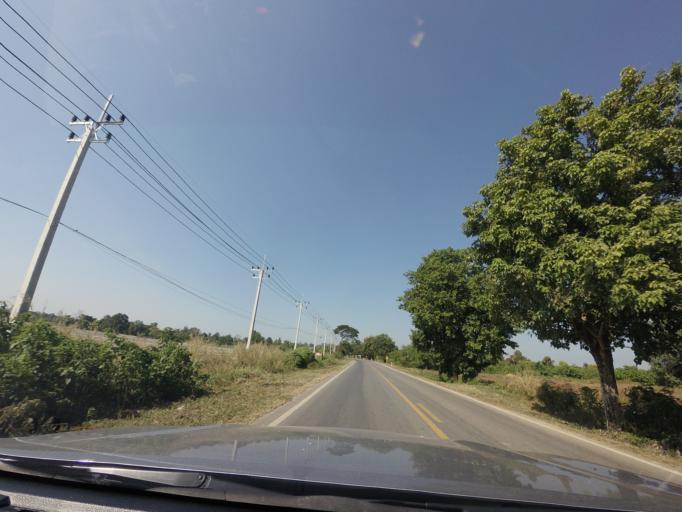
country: TH
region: Sukhothai
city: Sawankhalok
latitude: 17.3443
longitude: 99.8256
